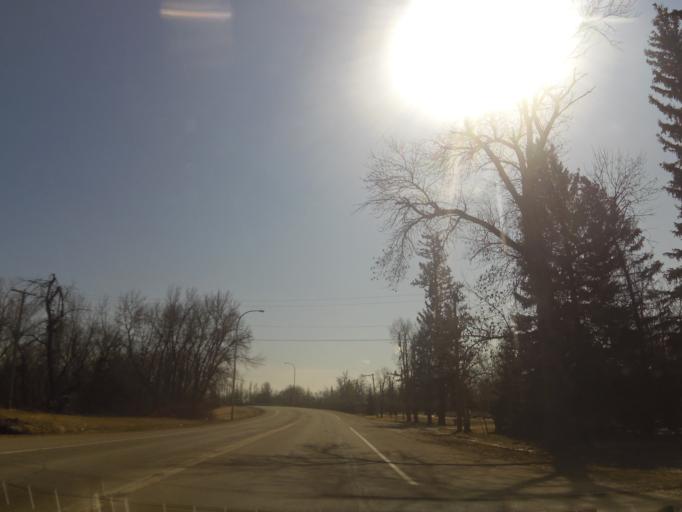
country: US
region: North Dakota
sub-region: Walsh County
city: Grafton
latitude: 48.2864
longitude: -97.3715
